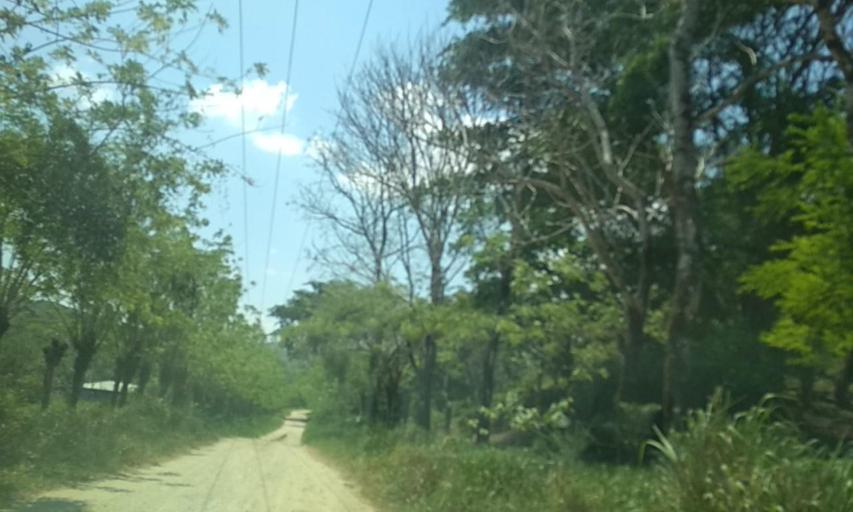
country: MX
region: Chiapas
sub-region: Tecpatan
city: Raudales Malpaso
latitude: 17.2835
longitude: -93.8329
